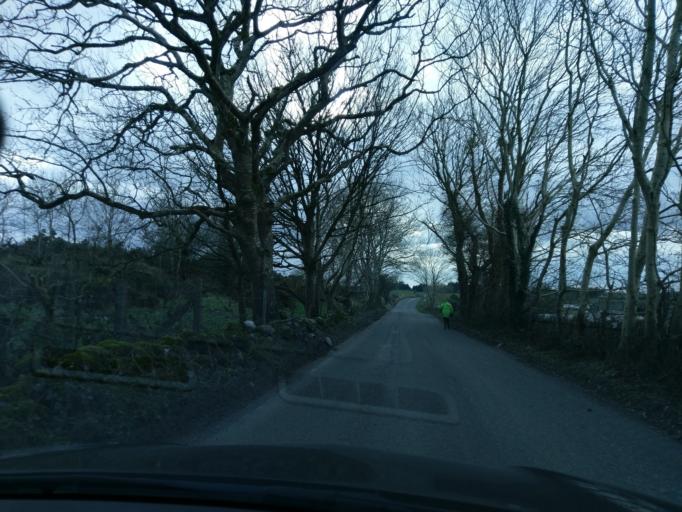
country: IE
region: Connaught
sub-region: County Galway
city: Athenry
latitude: 53.4886
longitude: -8.6140
